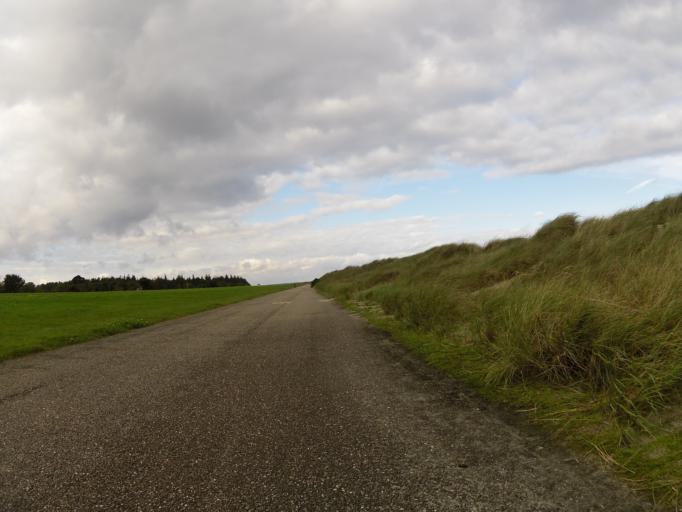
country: DE
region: Schleswig-Holstein
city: Wisch
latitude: 54.4327
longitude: 10.3489
